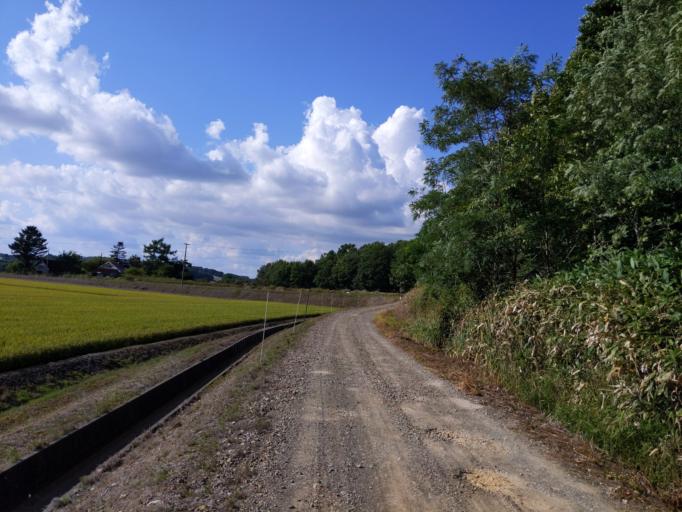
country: JP
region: Hokkaido
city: Iwamizawa
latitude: 43.1919
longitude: 141.8318
